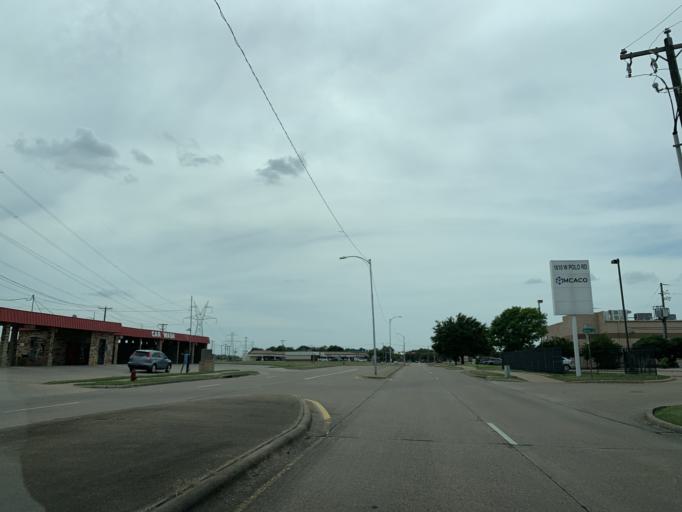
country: US
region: Texas
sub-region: Dallas County
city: Grand Prairie
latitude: 32.6584
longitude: -97.0244
